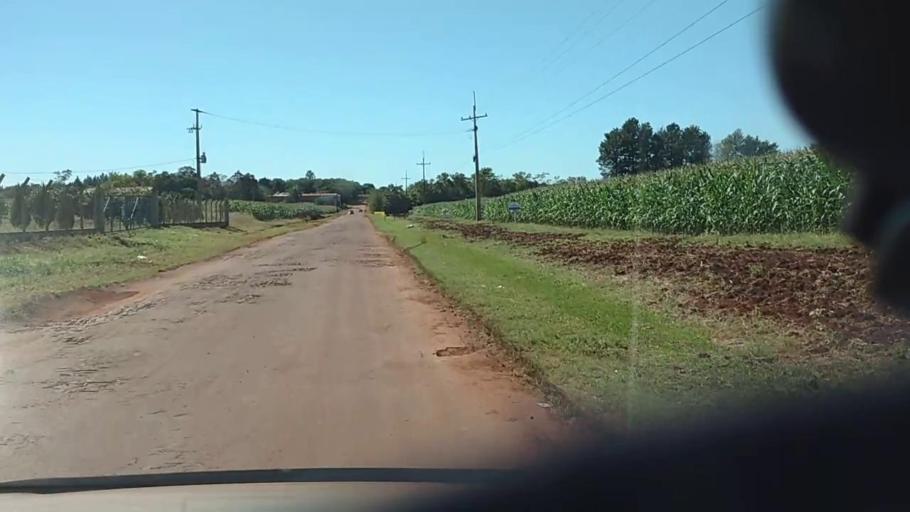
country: PY
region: Alto Parana
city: Naranjal
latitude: -25.9530
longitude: -55.1303
